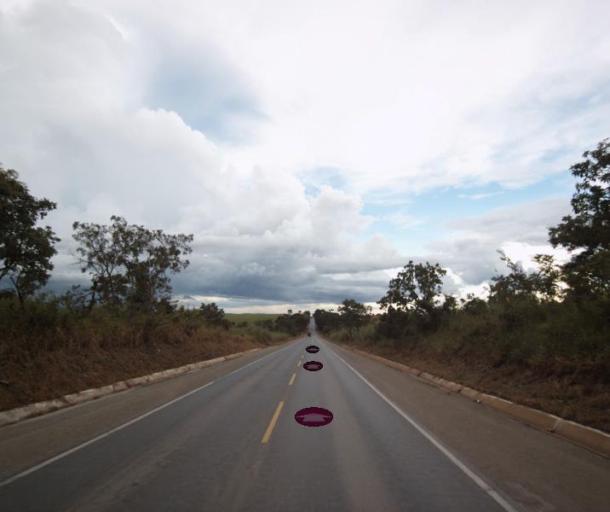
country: BR
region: Goias
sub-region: Itapaci
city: Itapaci
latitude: -14.8505
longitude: -49.3167
